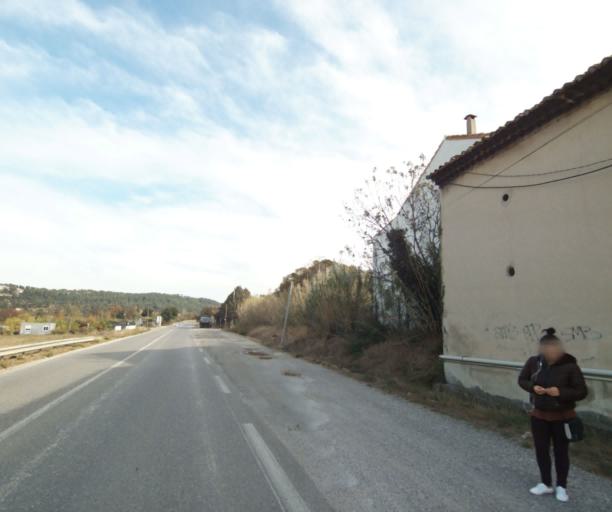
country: FR
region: Provence-Alpes-Cote d'Azur
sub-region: Departement des Bouches-du-Rhone
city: Les Pennes-Mirabeau
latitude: 43.4051
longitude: 5.2829
